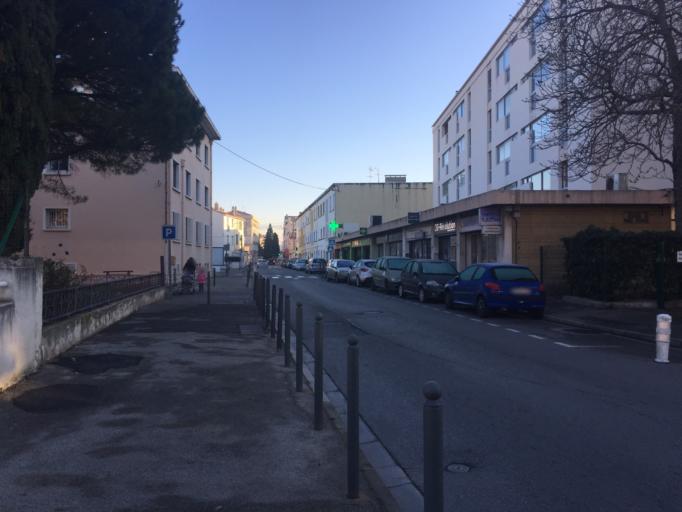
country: FR
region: Provence-Alpes-Cote d'Azur
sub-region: Departement des Bouches-du-Rhone
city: Marignane
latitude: 43.4177
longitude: 5.2123
